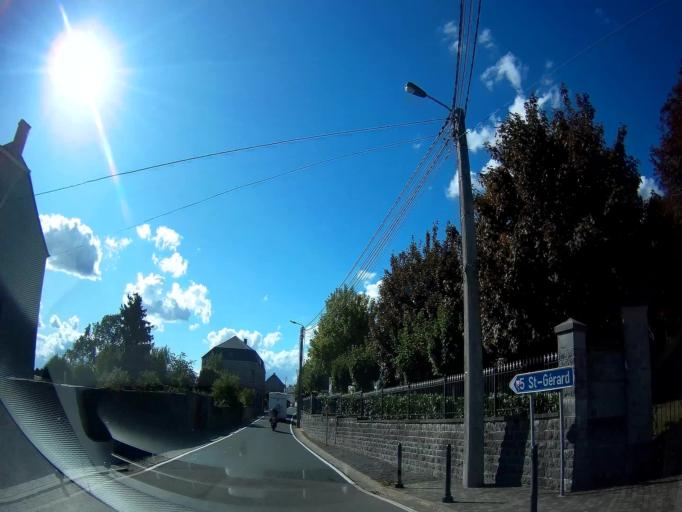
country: BE
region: Wallonia
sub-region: Province de Namur
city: Mettet
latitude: 50.3181
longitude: 4.7520
